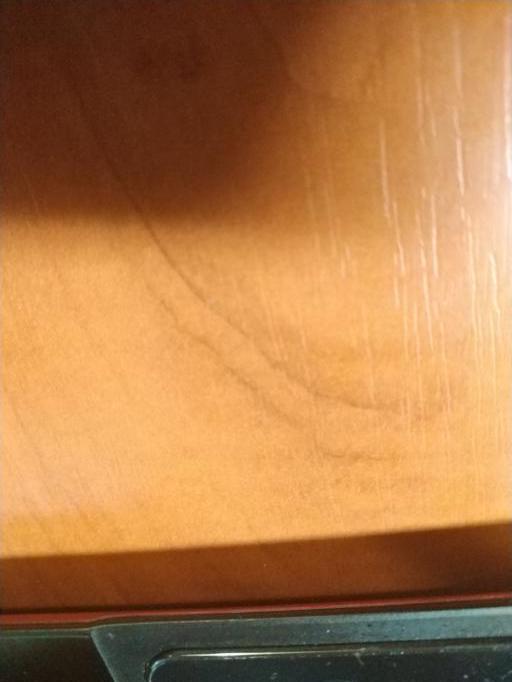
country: RU
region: Tverskaya
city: Likhoslavl'
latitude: 57.1279
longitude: 35.4644
